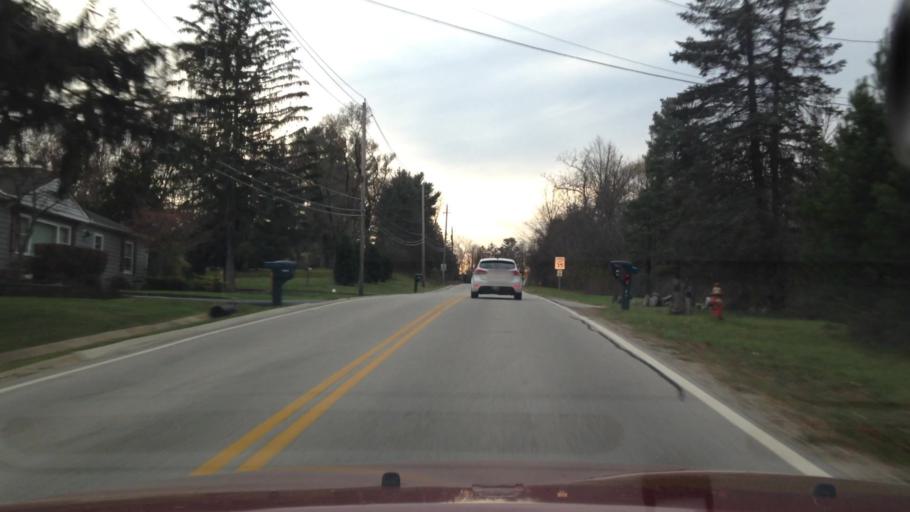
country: US
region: Ohio
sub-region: Cuyahoga County
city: Walton Hills
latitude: 41.3679
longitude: -81.5500
